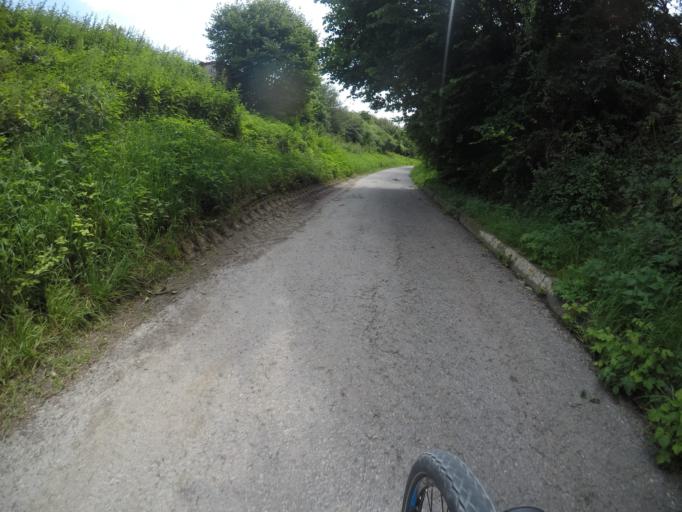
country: DE
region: Baden-Wuerttemberg
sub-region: Freiburg Region
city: Zimmern ob Rottweil
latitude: 48.1755
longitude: 8.6038
